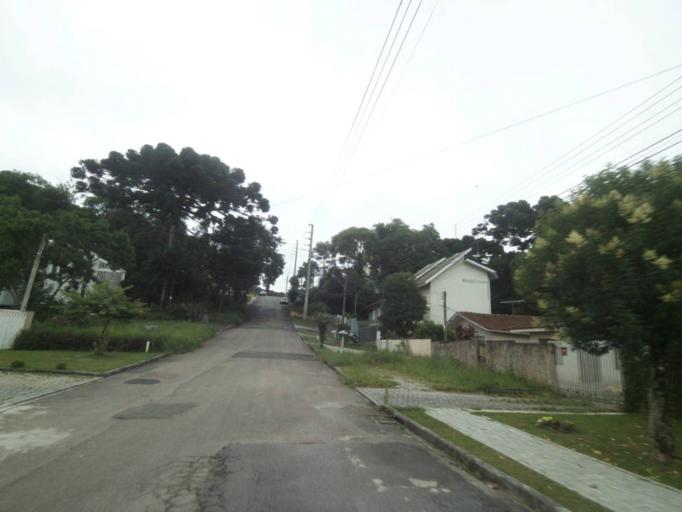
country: BR
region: Parana
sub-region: Curitiba
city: Curitiba
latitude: -25.4475
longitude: -49.3165
